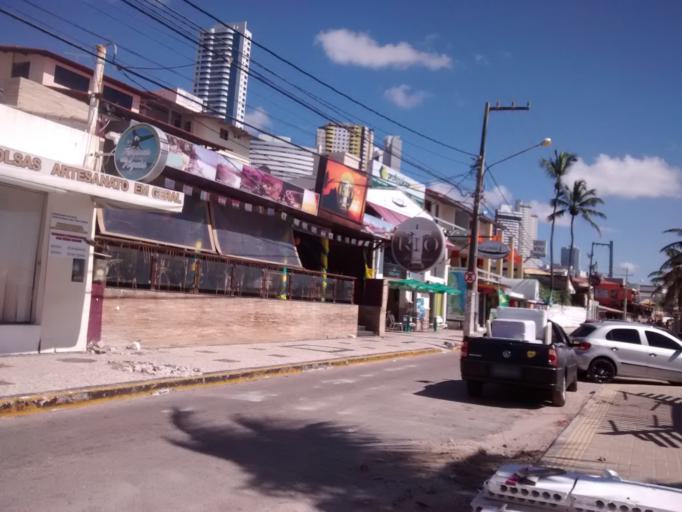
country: BR
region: Rio Grande do Norte
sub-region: Natal
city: Natal
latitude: -5.8800
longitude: -35.1728
